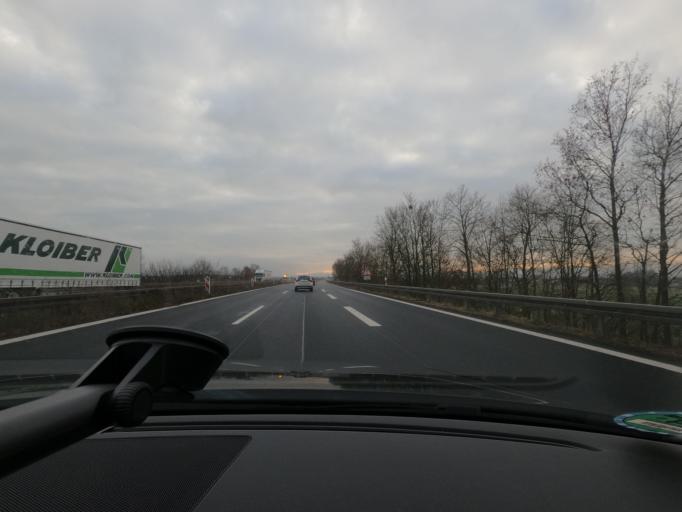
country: DE
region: Bavaria
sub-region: Upper Franconia
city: Kemmern
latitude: 49.9622
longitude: 10.8821
